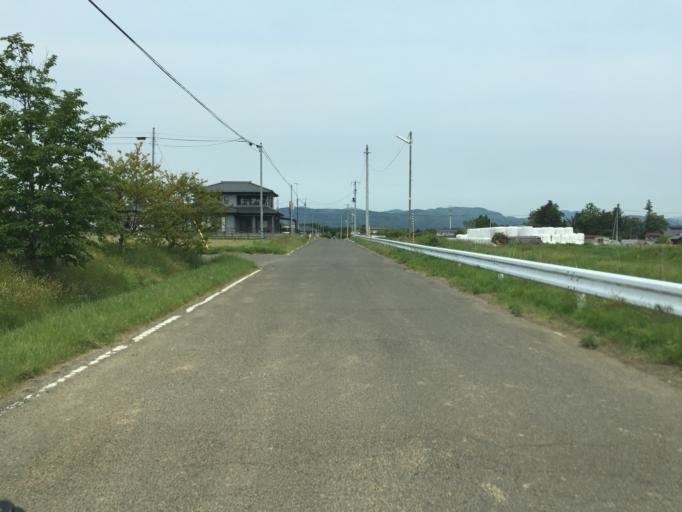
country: JP
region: Fukushima
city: Fukushima-shi
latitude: 37.7270
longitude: 140.4020
